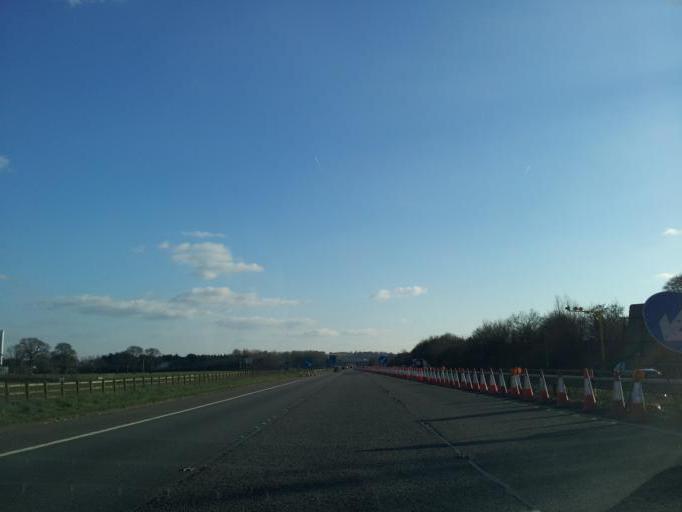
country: GB
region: England
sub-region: Devon
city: Cullompton
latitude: 50.8690
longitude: -3.3824
